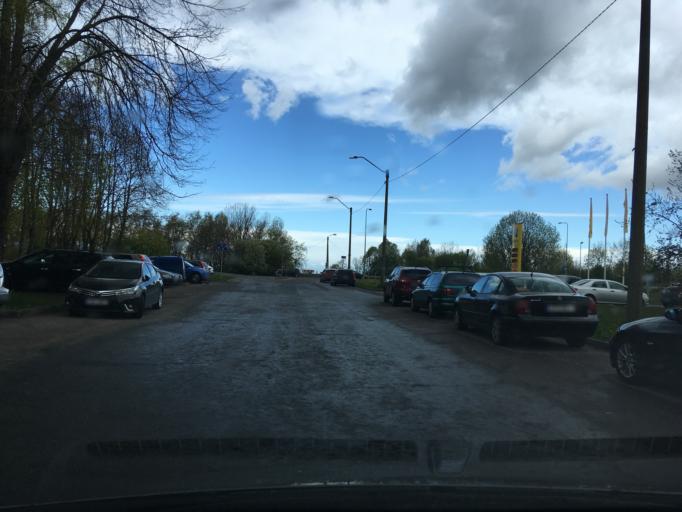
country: EE
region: Harju
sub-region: Tallinna linn
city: Kose
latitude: 59.4511
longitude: 24.8534
